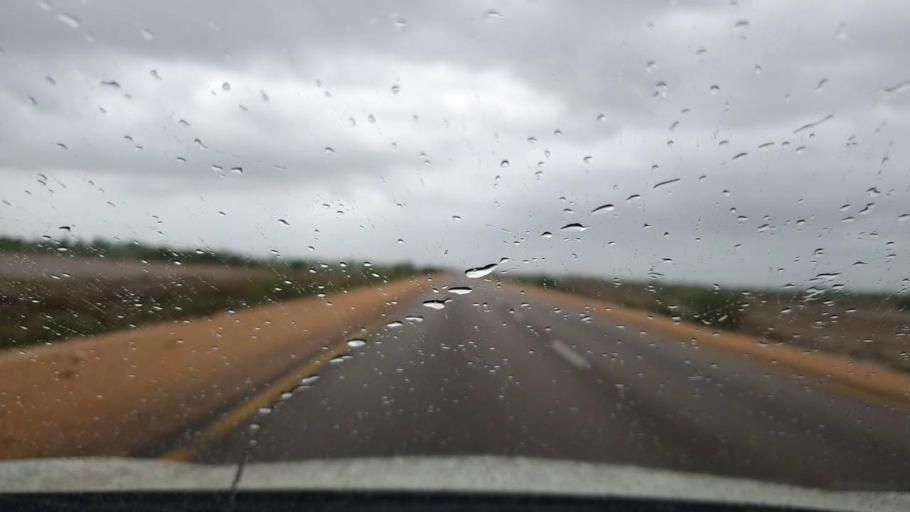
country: PK
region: Sindh
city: Badin
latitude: 24.6563
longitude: 68.6894
